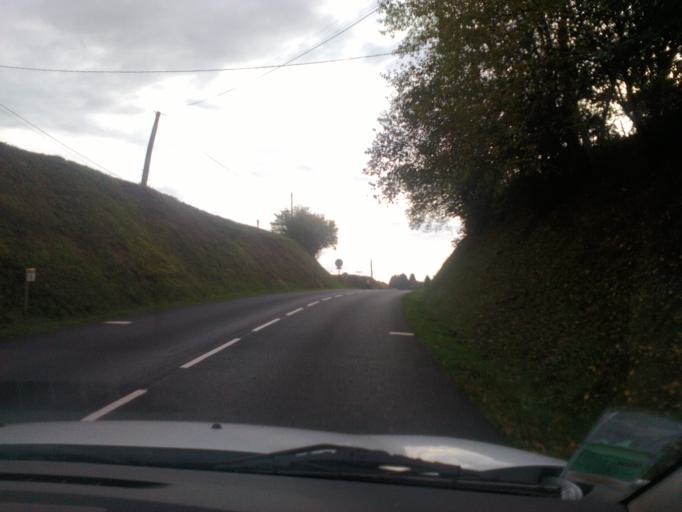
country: FR
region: Lorraine
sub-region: Departement des Vosges
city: Granges-sur-Vologne
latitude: 48.1810
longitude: 6.8111
